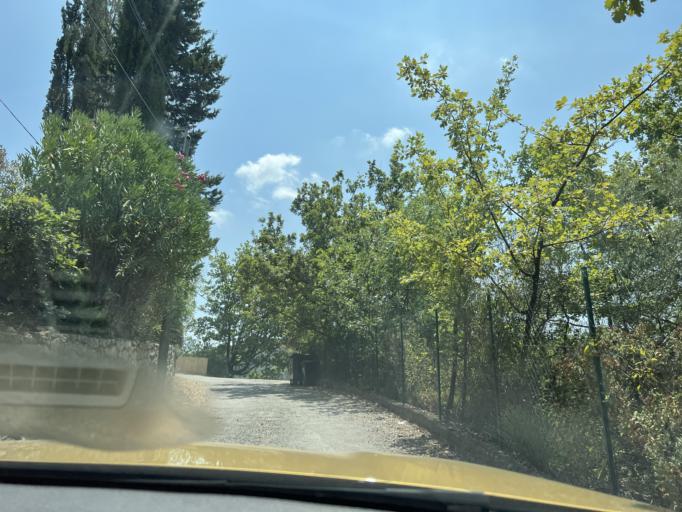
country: FR
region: Provence-Alpes-Cote d'Azur
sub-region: Departement des Alpes-Maritimes
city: Tourrettes-sur-Loup
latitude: 43.7052
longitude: 7.0274
